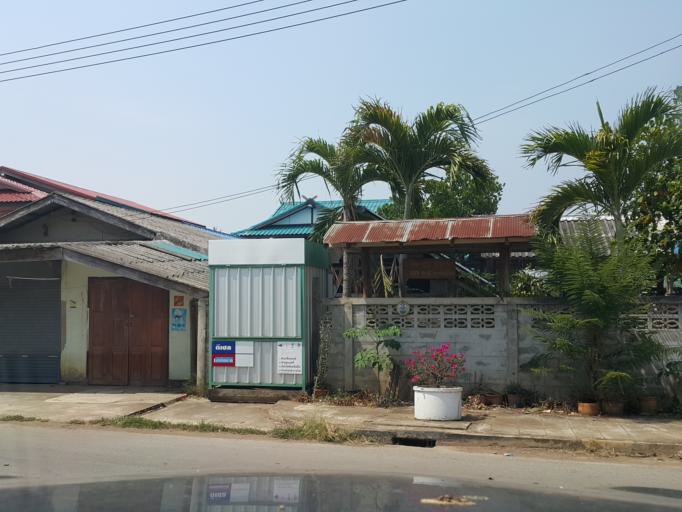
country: TH
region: Sukhothai
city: Thung Saliam
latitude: 17.3131
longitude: 99.5455
